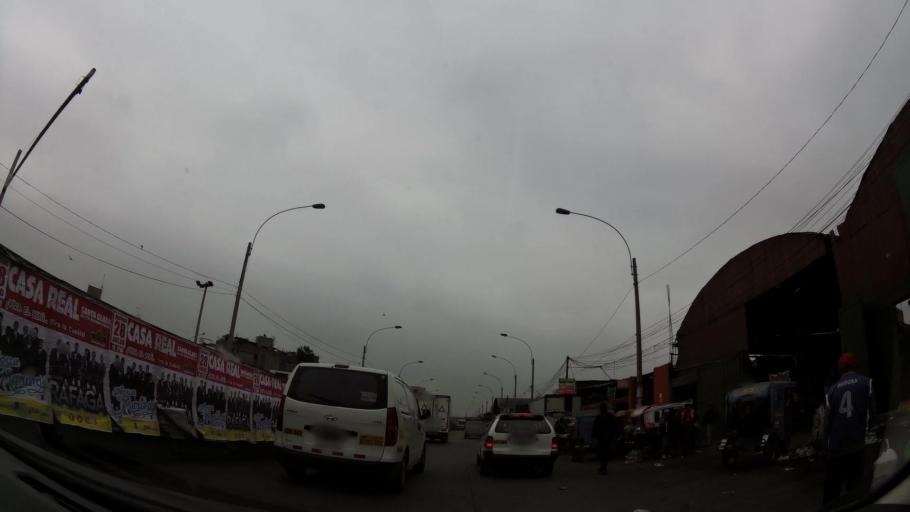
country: PE
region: Lima
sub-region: Lima
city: San Luis
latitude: -12.0589
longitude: -77.0083
